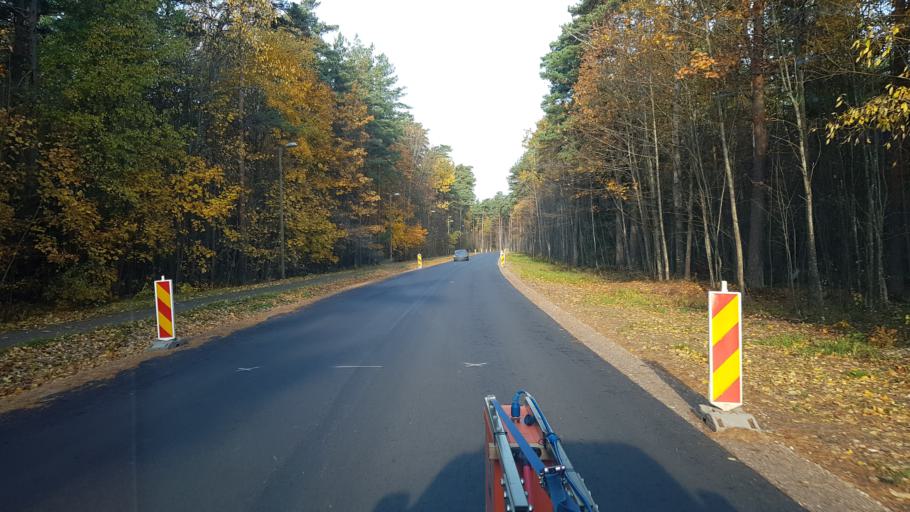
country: EE
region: Paernumaa
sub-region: Paikuse vald
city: Paikuse
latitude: 58.3642
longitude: 24.6044
